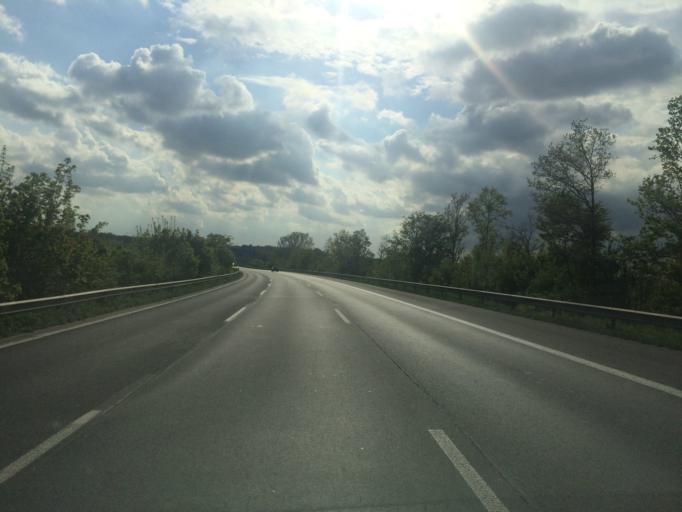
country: DE
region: North Rhine-Westphalia
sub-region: Regierungsbezirk Detmold
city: Vlotho
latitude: 52.2109
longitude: 8.8594
